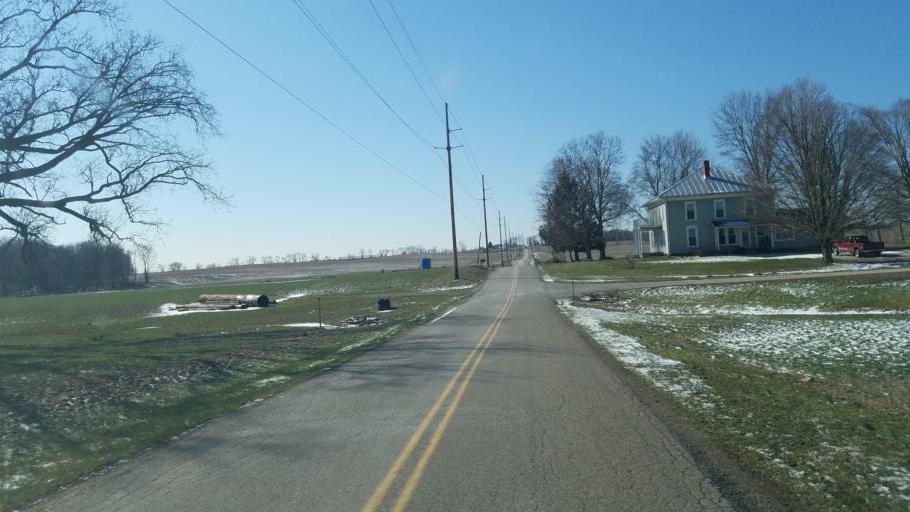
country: US
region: Ohio
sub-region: Licking County
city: Utica
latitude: 40.2964
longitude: -82.4738
